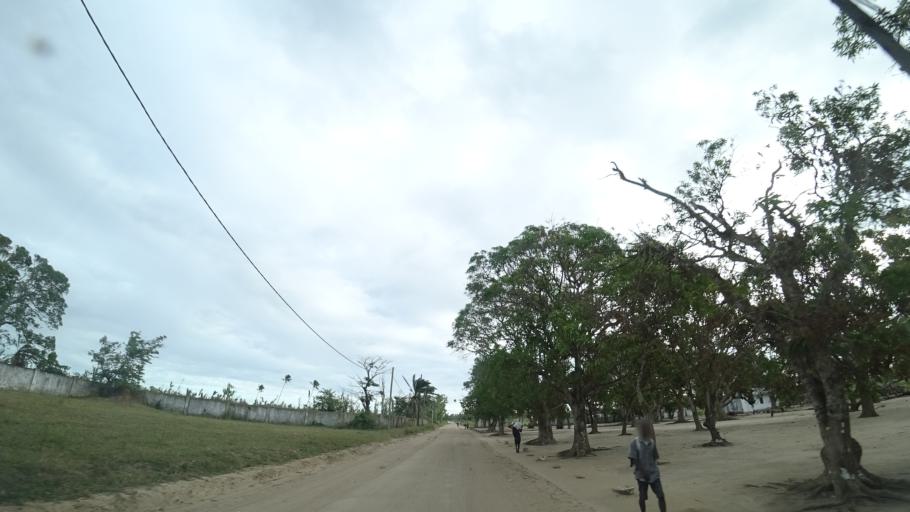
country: MZ
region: Sofala
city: Beira
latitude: -19.7675
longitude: 34.8927
